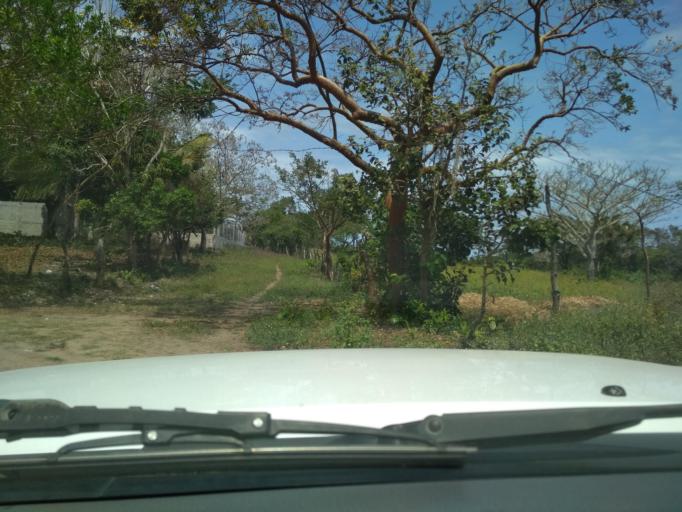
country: MX
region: Veracruz
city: Anton Lizardo
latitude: 19.0072
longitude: -95.9883
